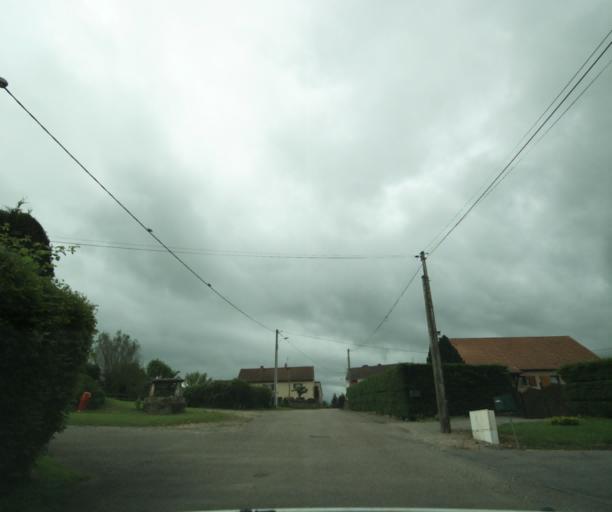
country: FR
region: Bourgogne
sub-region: Departement de Saone-et-Loire
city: Charolles
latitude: 46.4421
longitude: 4.2771
